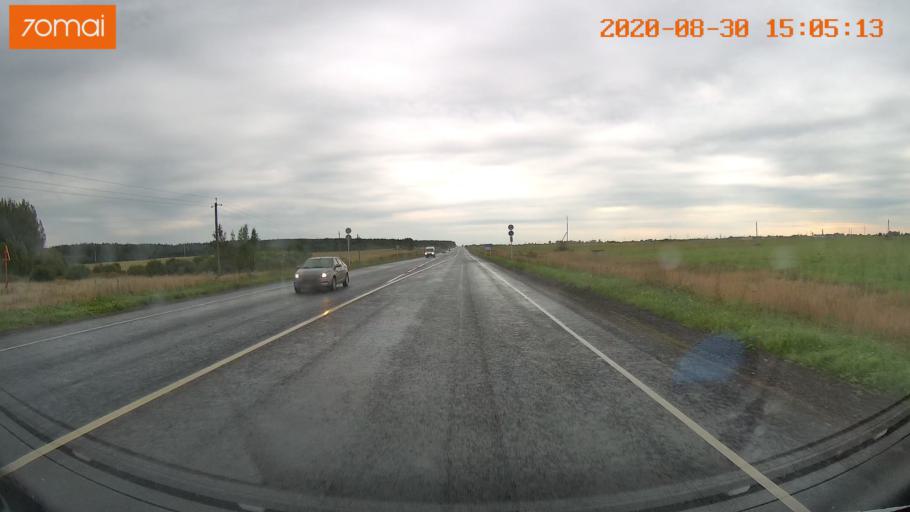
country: RU
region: Ivanovo
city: Staraya Vichuga
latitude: 57.2766
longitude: 41.9083
